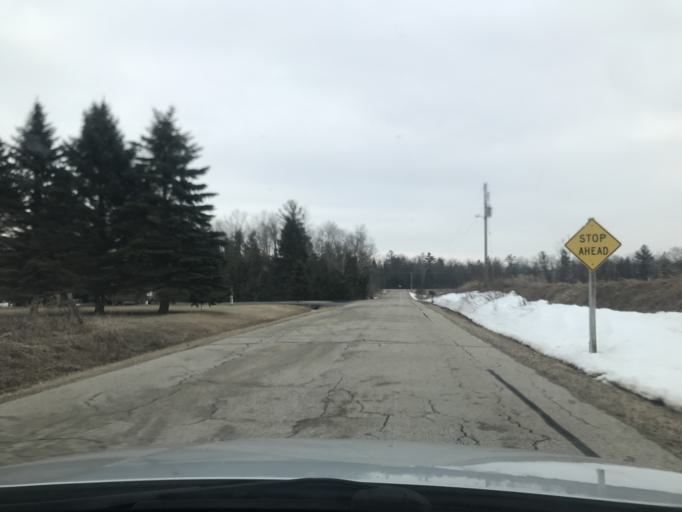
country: US
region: Wisconsin
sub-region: Marinette County
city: Peshtigo
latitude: 45.1117
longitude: -88.0082
